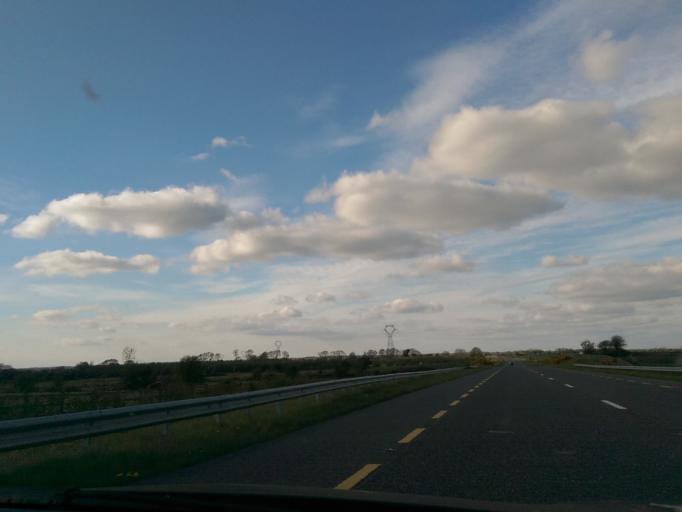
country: IE
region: Connaught
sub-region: County Galway
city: Loughrea
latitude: 53.2372
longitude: -8.5943
